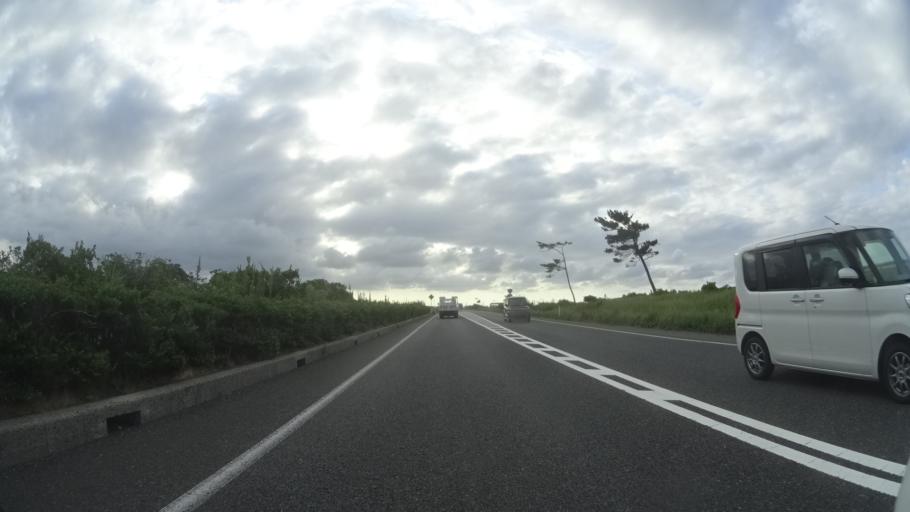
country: JP
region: Tottori
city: Kurayoshi
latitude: 35.5000
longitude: 133.7497
